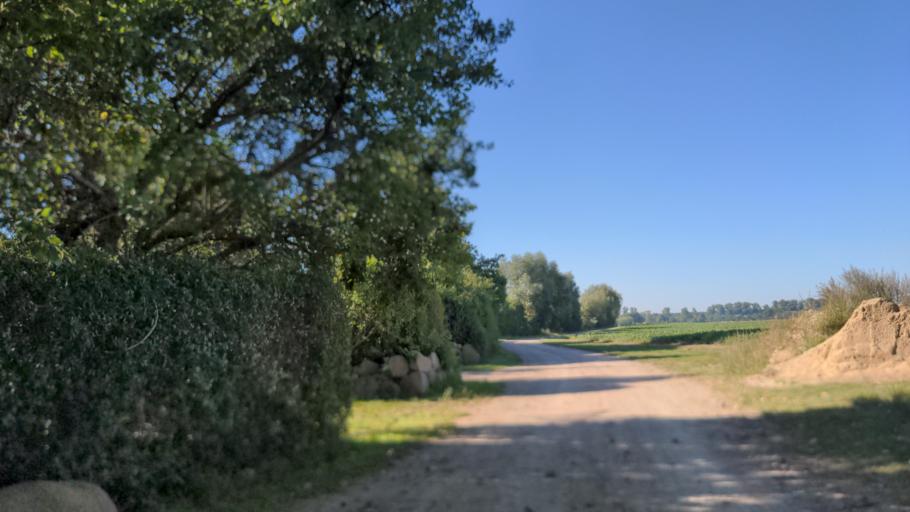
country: DE
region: Mecklenburg-Vorpommern
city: Ostseebad Boltenhagen
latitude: 53.9550
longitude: 11.2381
